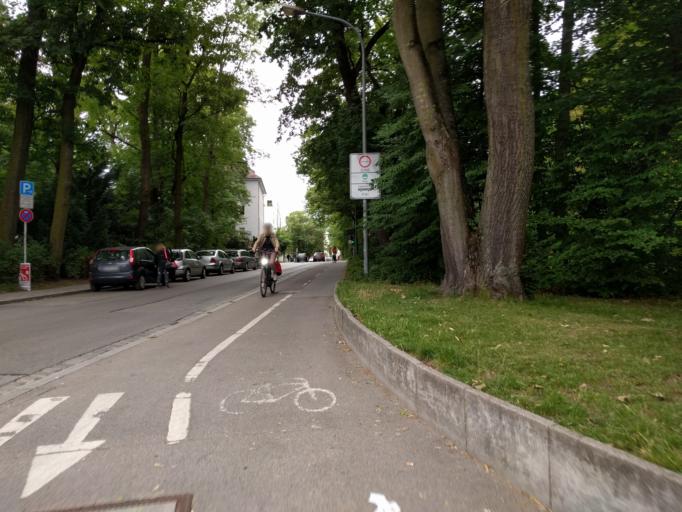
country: DE
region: Bavaria
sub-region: Upper Palatinate
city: Regensburg
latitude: 49.0136
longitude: 12.0997
